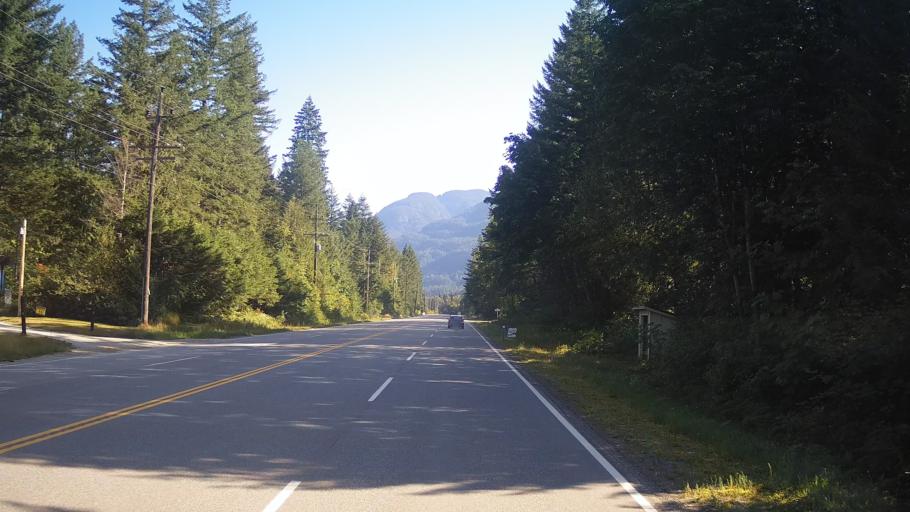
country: CA
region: British Columbia
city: Hope
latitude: 49.4713
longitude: -121.4282
